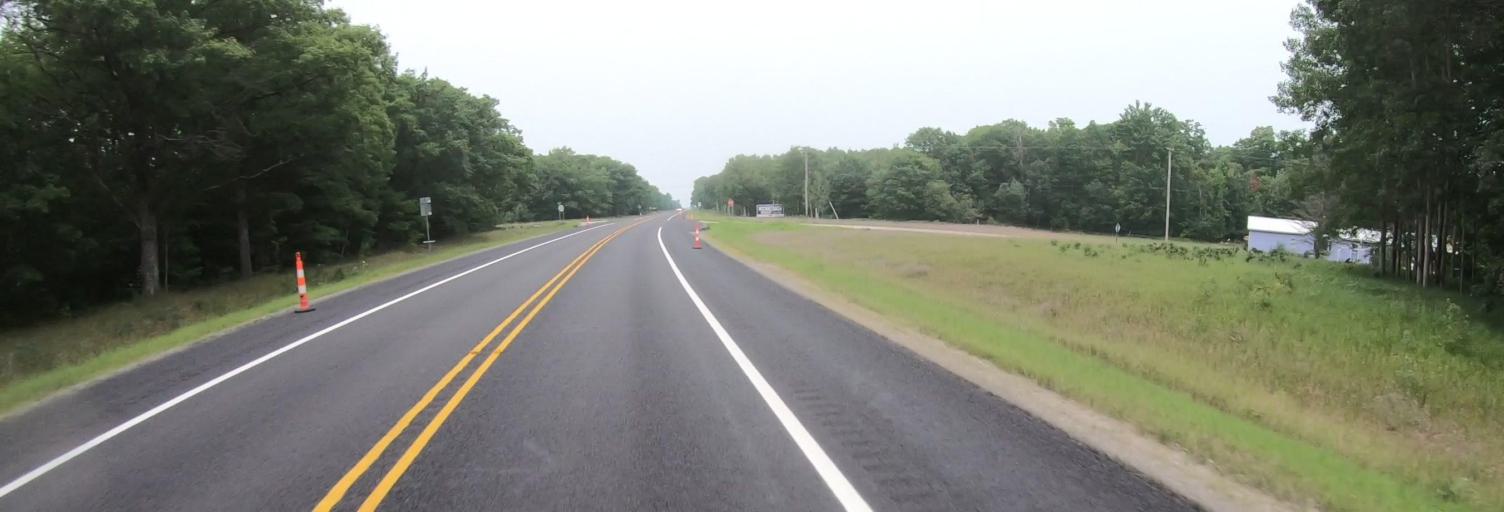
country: US
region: Michigan
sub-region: Mackinac County
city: Saint Ignace
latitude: 45.7024
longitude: -84.7718
